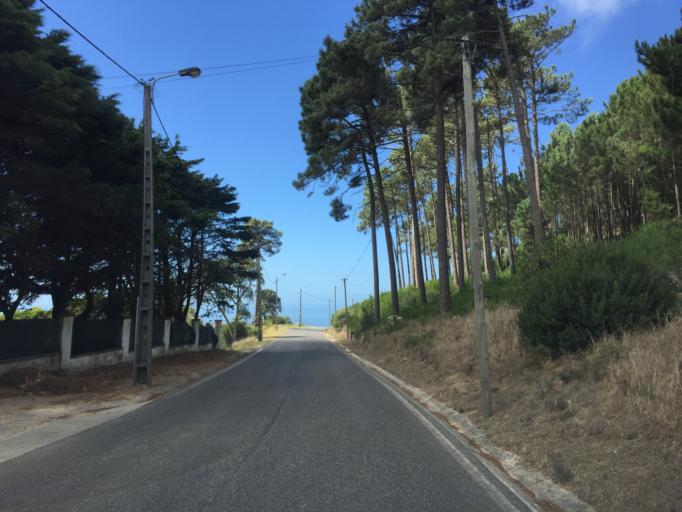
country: PT
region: Lisbon
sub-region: Cascais
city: Alcabideche
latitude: 38.7586
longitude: -9.4387
